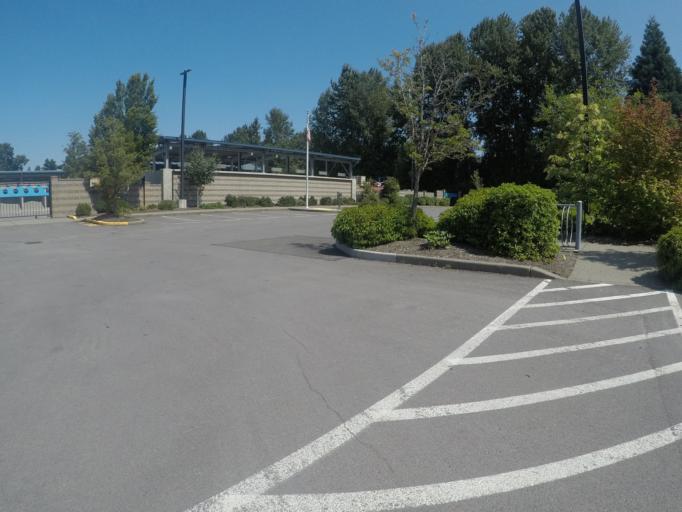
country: US
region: Washington
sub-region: King County
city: Kenmore
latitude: 47.7626
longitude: -122.2479
